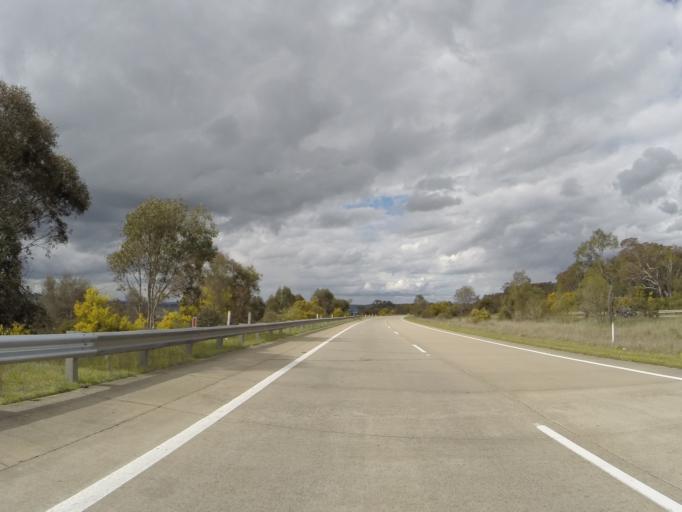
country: AU
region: New South Wales
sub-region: Goulburn Mulwaree
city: Goulburn
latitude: -34.8044
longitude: 149.4927
